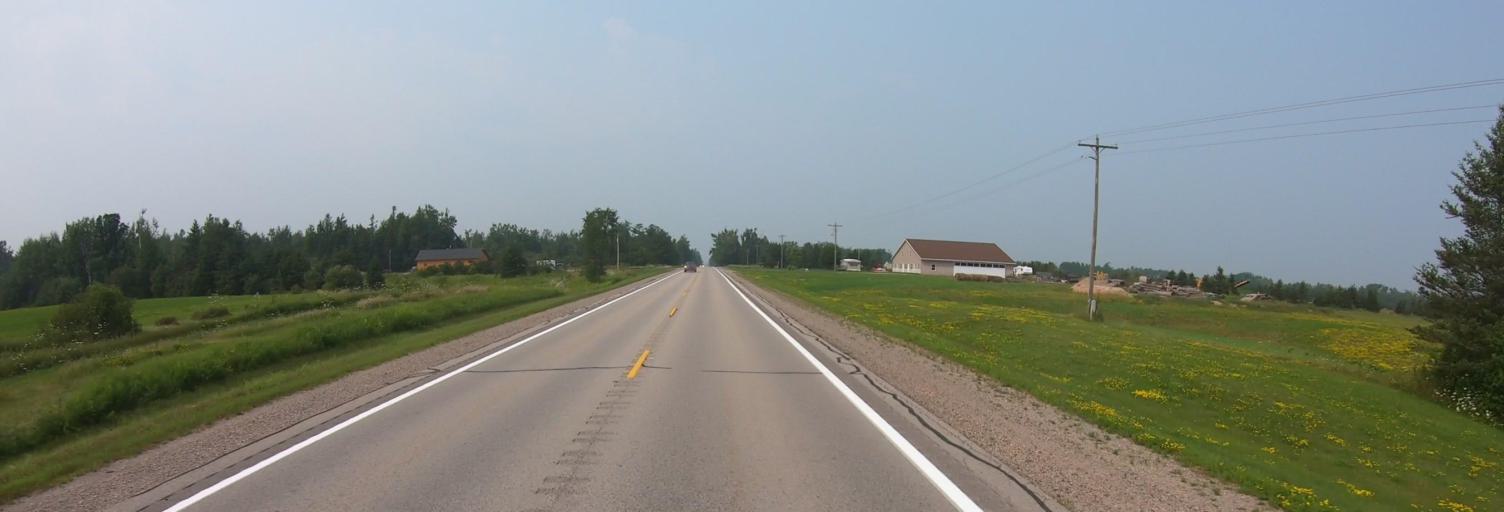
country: US
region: Michigan
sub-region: Chippewa County
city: Sault Ste. Marie
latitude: 46.2363
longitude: -84.3634
